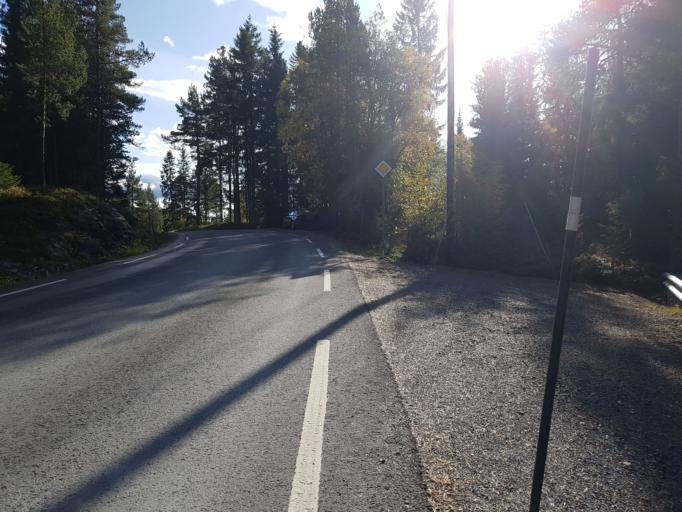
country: NO
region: Sor-Trondelag
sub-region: Malvik
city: Malvik
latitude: 63.3824
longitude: 10.5973
